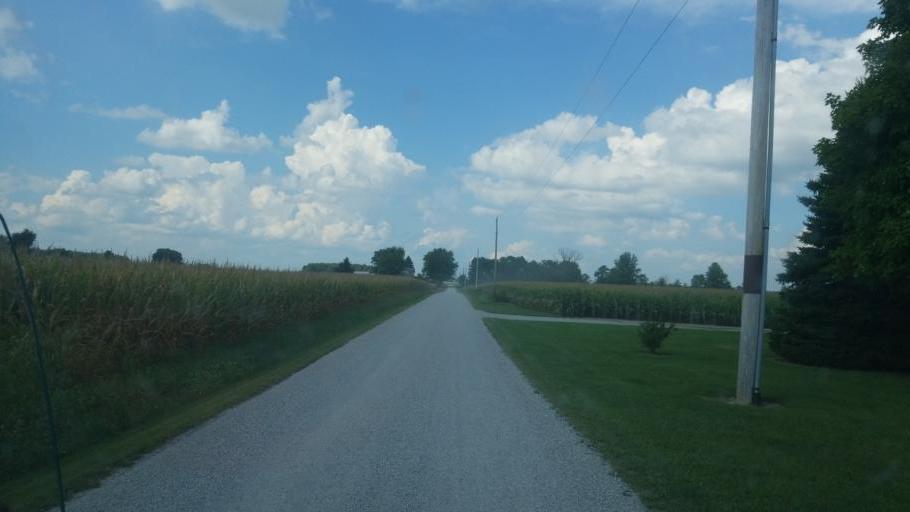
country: US
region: Ohio
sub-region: Huron County
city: Willard
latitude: 40.9901
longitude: -82.7966
